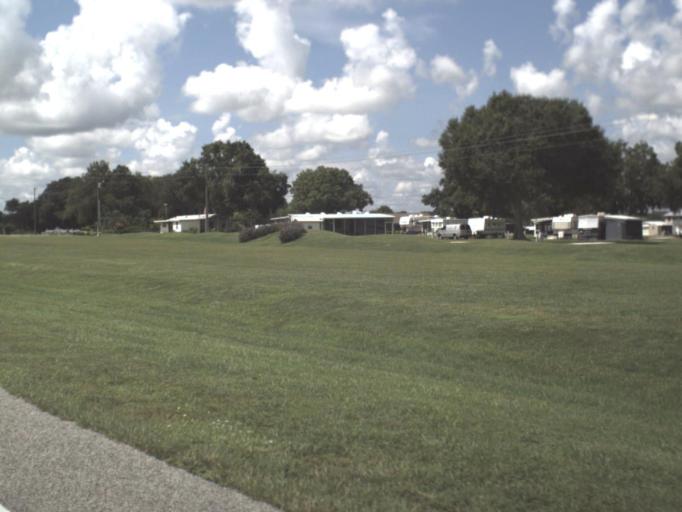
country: US
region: Florida
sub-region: DeSoto County
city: Arcadia
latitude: 27.3104
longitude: -81.8186
